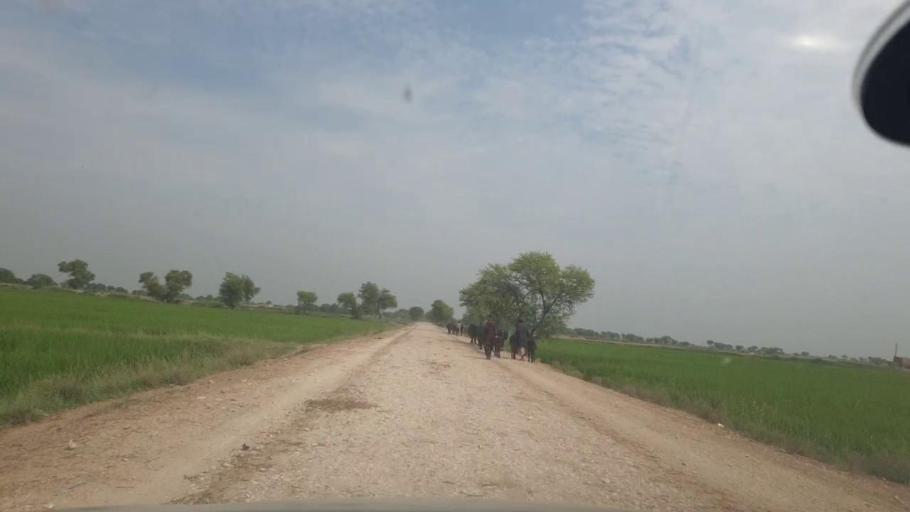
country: PK
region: Sindh
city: Jacobabad
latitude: 28.2459
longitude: 68.5417
